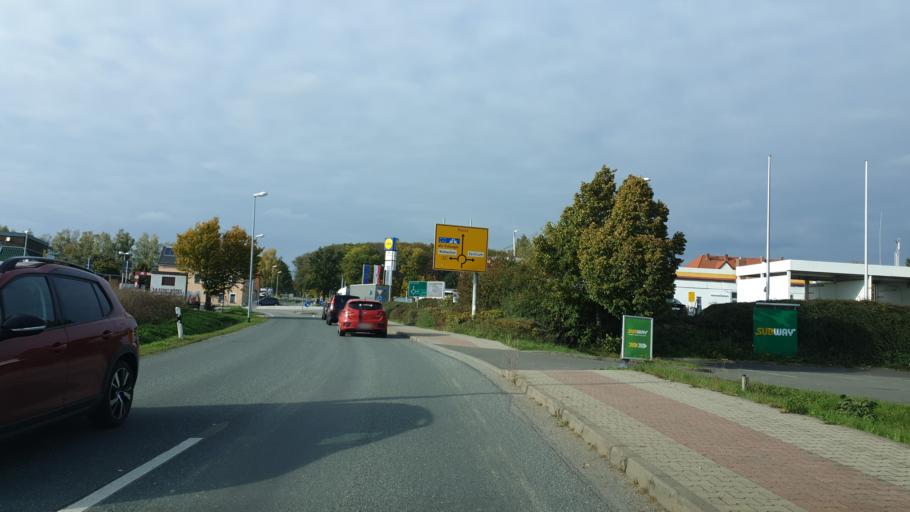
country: DE
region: Saxony
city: Meerane
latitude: 50.8414
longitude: 12.4456
